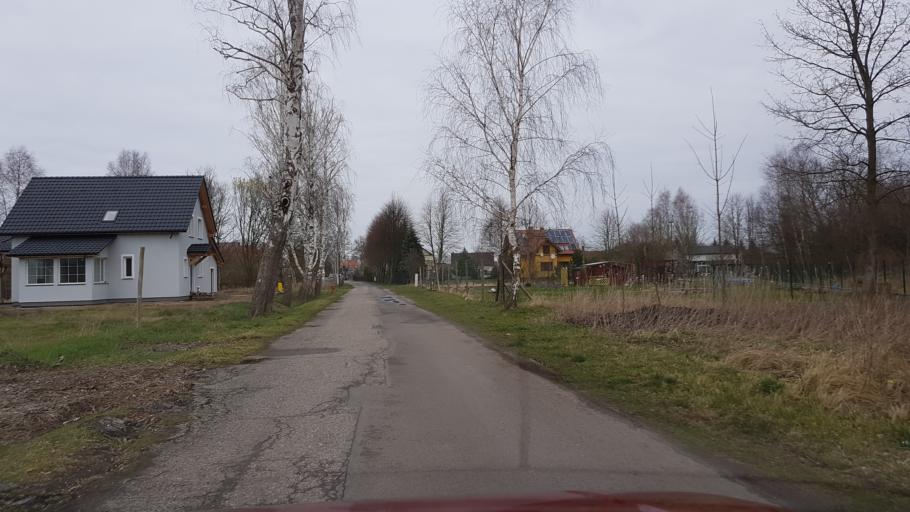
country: PL
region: West Pomeranian Voivodeship
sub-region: Powiat goleniowski
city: Stepnica
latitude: 53.6528
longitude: 14.5146
